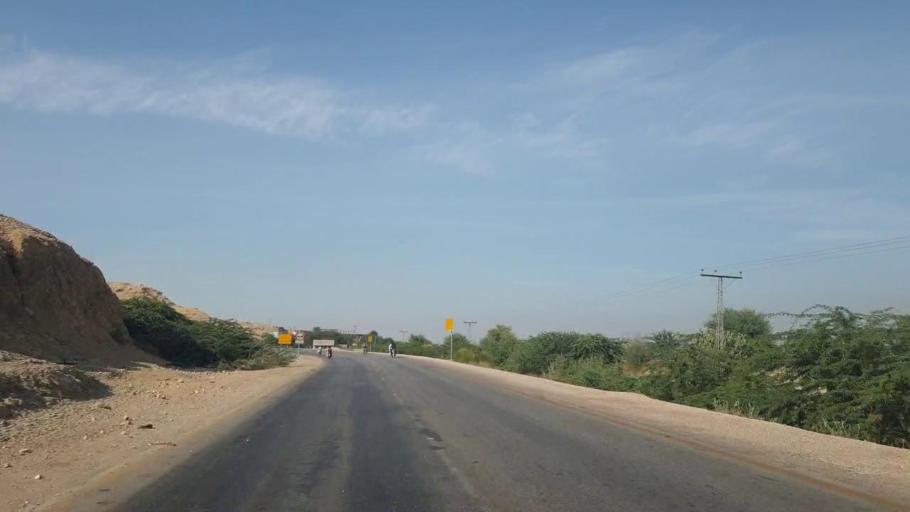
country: PK
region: Sindh
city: Sehwan
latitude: 26.3134
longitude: 67.8915
